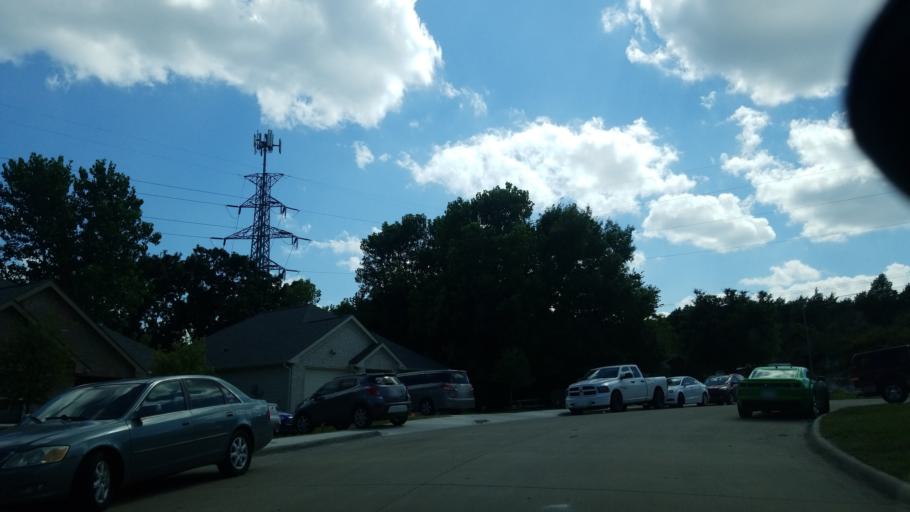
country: US
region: Texas
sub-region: Dallas County
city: Balch Springs
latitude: 32.7618
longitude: -96.6990
